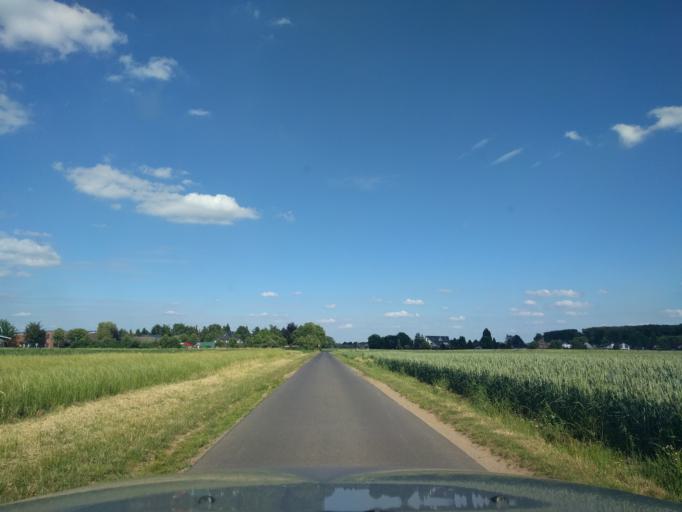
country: DE
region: North Rhine-Westphalia
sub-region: Regierungsbezirk Dusseldorf
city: Willich
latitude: 51.2442
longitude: 6.5061
